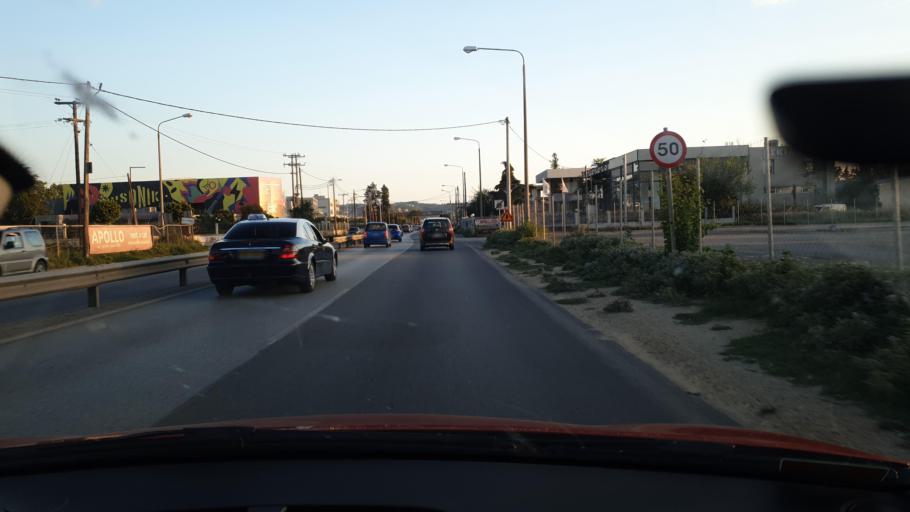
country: GR
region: Central Macedonia
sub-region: Nomos Thessalonikis
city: Neo Rysi
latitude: 40.5264
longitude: 22.9948
